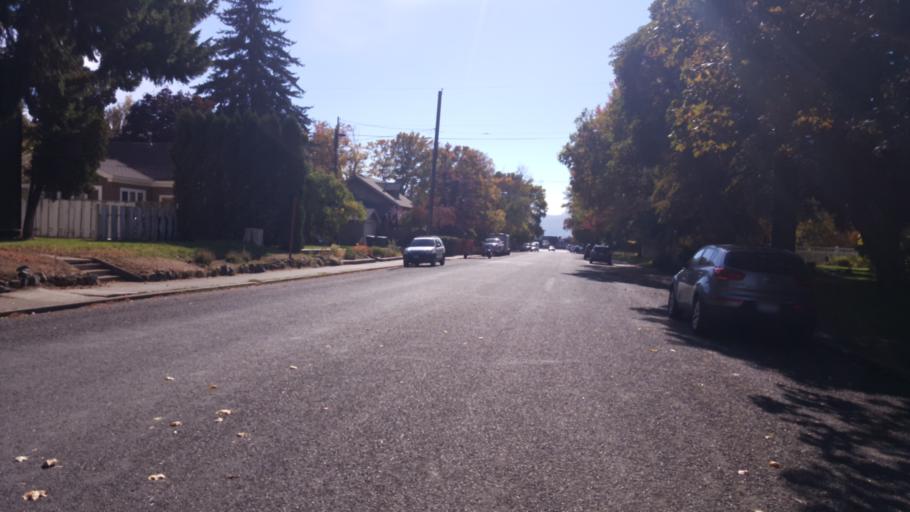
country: US
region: Washington
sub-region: Kittitas County
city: Ellensburg
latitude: 47.0017
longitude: -120.5471
